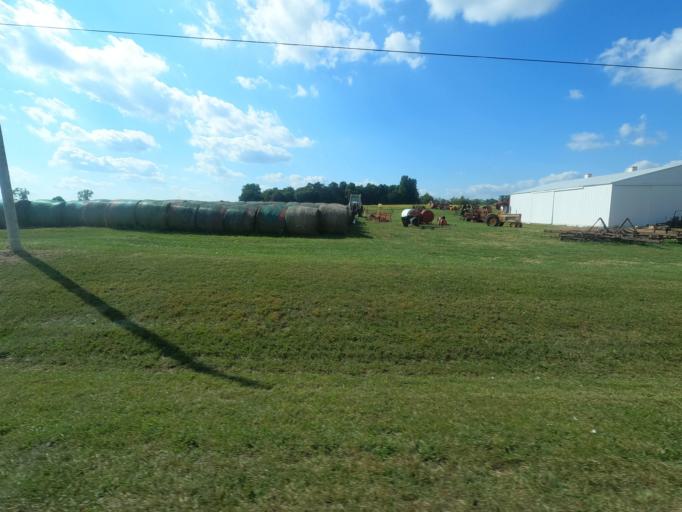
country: US
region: Illinois
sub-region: Massac County
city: Metropolis
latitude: 37.1865
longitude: -88.6766
